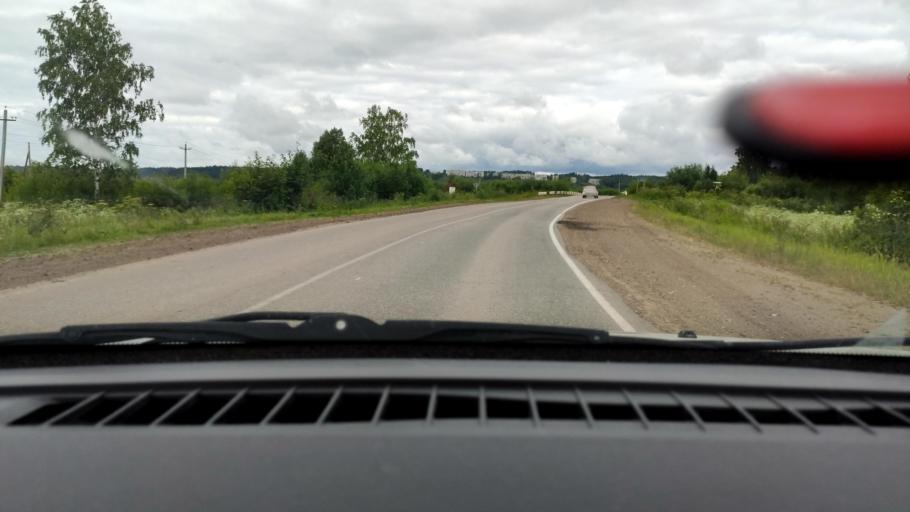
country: RU
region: Perm
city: Chaykovskaya
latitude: 58.0937
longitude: 55.5982
